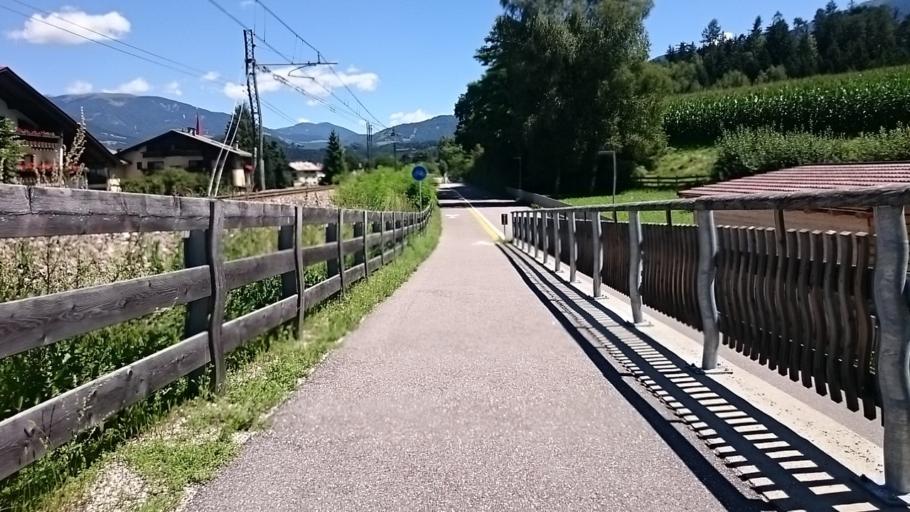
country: IT
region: Trentino-Alto Adige
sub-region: Bolzano
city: San Lorenzo di Sebato
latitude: 46.7821
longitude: 11.8961
